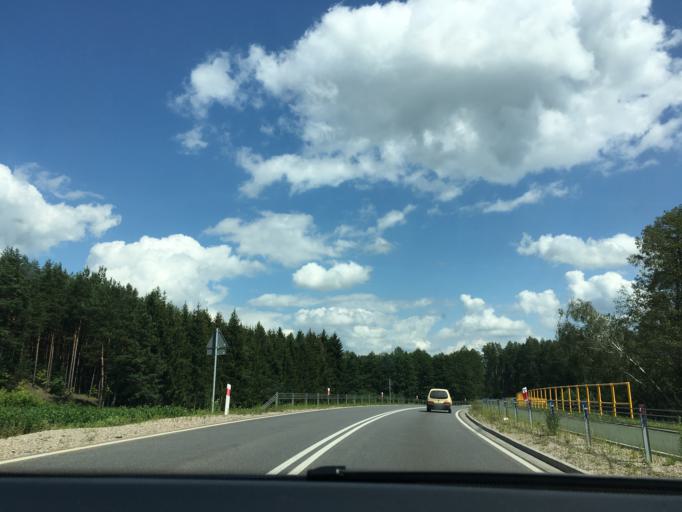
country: PL
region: Podlasie
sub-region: Powiat sejnenski
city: Krasnopol
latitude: 54.0905
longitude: 23.1335
